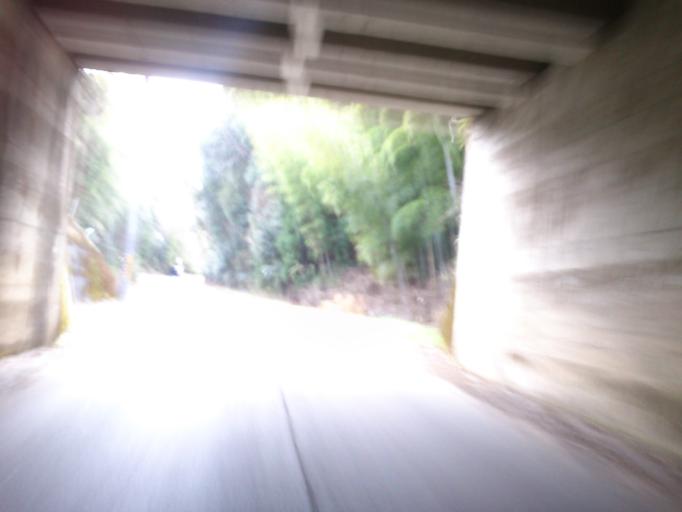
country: JP
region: Mie
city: Ueno-ebisumachi
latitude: 34.7309
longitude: 136.0013
